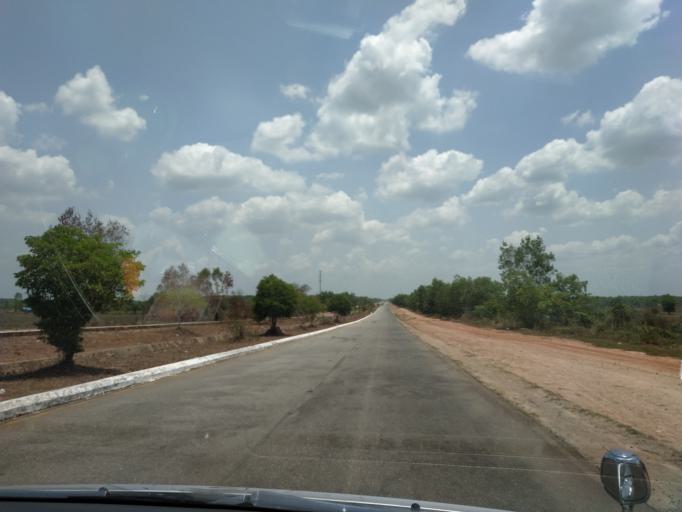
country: MM
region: Bago
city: Thanatpin
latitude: 17.2537
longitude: 96.2300
